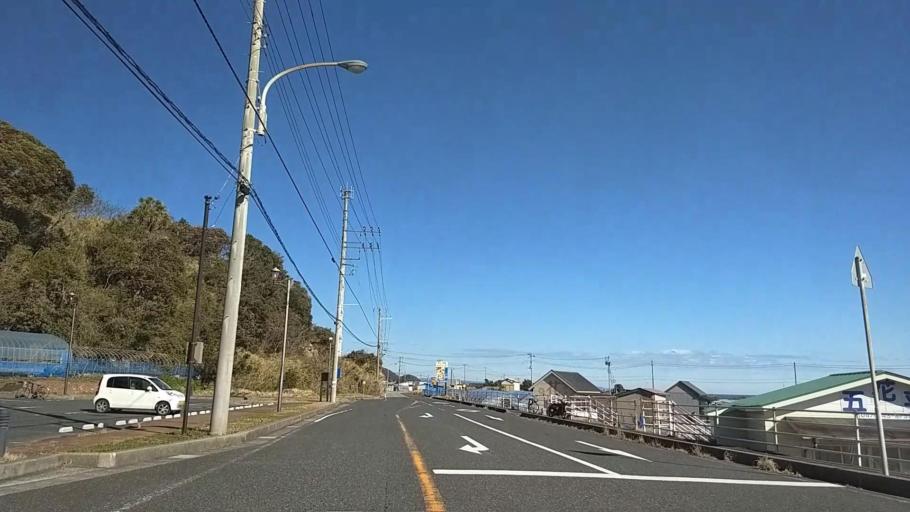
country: JP
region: Chiba
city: Tateyama
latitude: 34.9183
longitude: 139.9357
